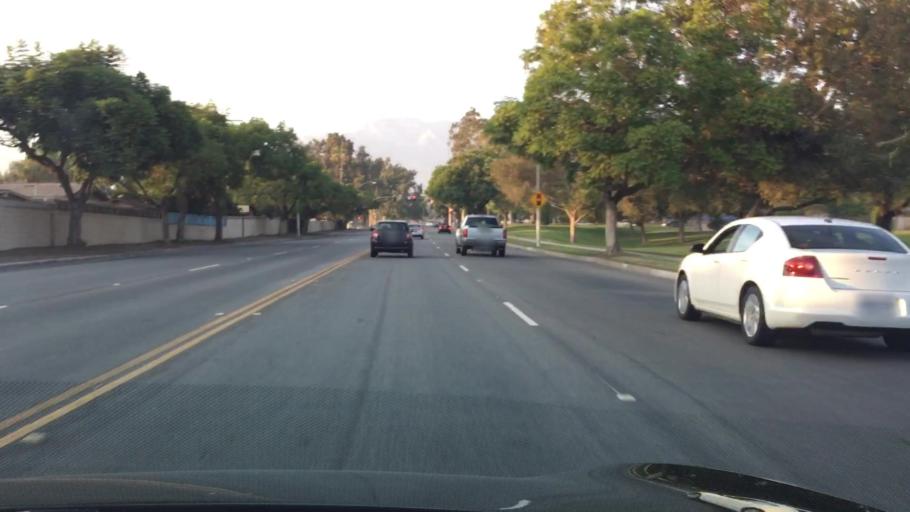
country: US
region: California
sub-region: San Bernardino County
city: Ontario
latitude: 34.0725
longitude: -117.6296
